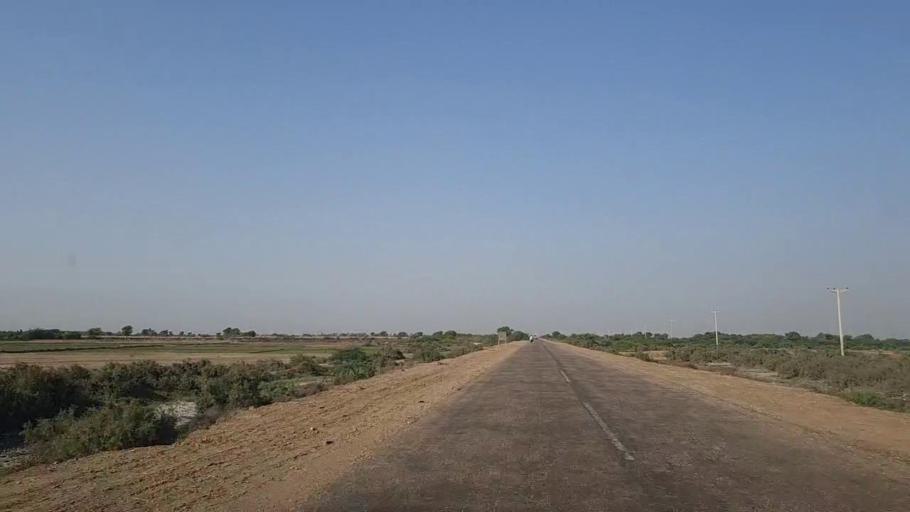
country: PK
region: Sindh
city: Mirpur Batoro
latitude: 24.6186
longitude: 68.4057
